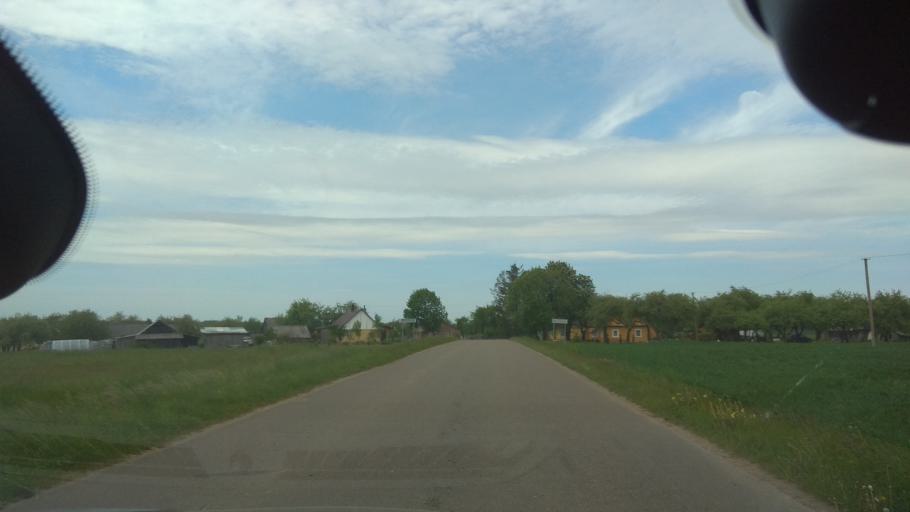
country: LT
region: Vilnius County
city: Ukmerge
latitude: 55.1042
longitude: 24.6881
